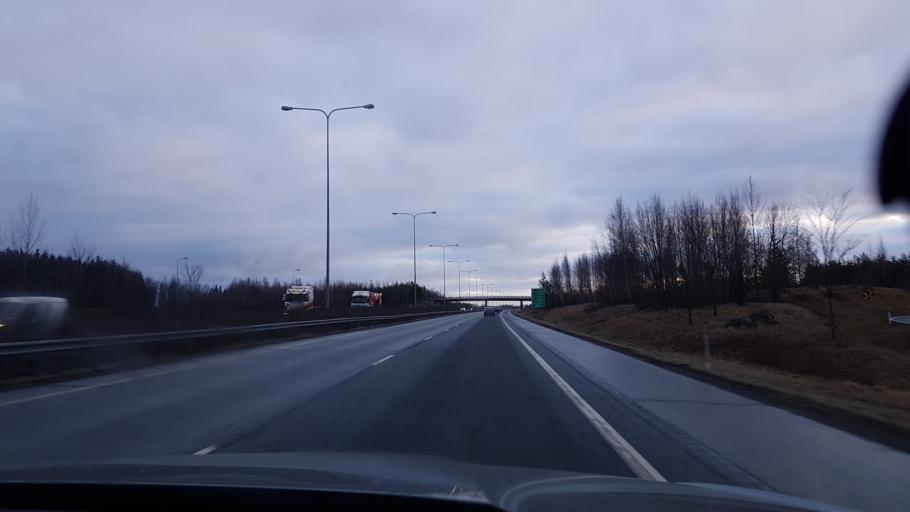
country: FI
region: Pirkanmaa
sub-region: Etelae-Pirkanmaa
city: Toijala
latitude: 61.2216
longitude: 23.8388
